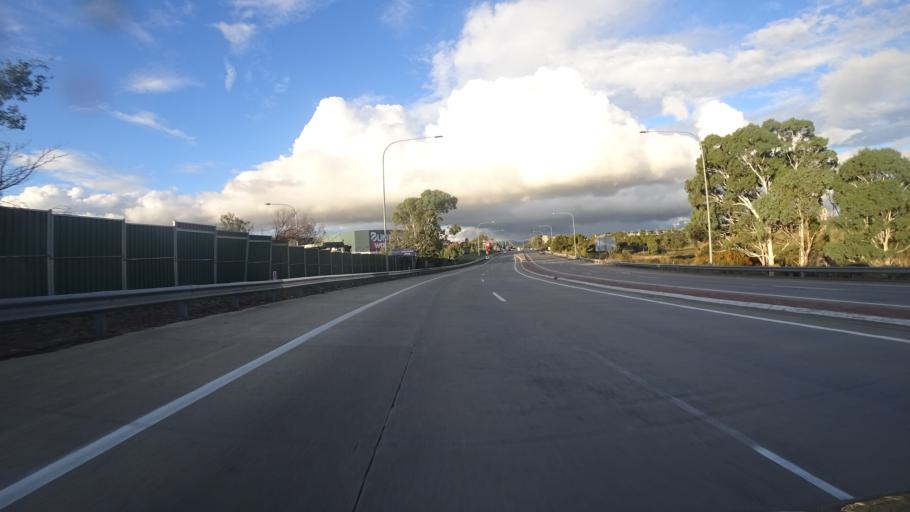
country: AU
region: New South Wales
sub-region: Goulburn Mulwaree
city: Goulburn
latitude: -34.7747
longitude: 149.6877
